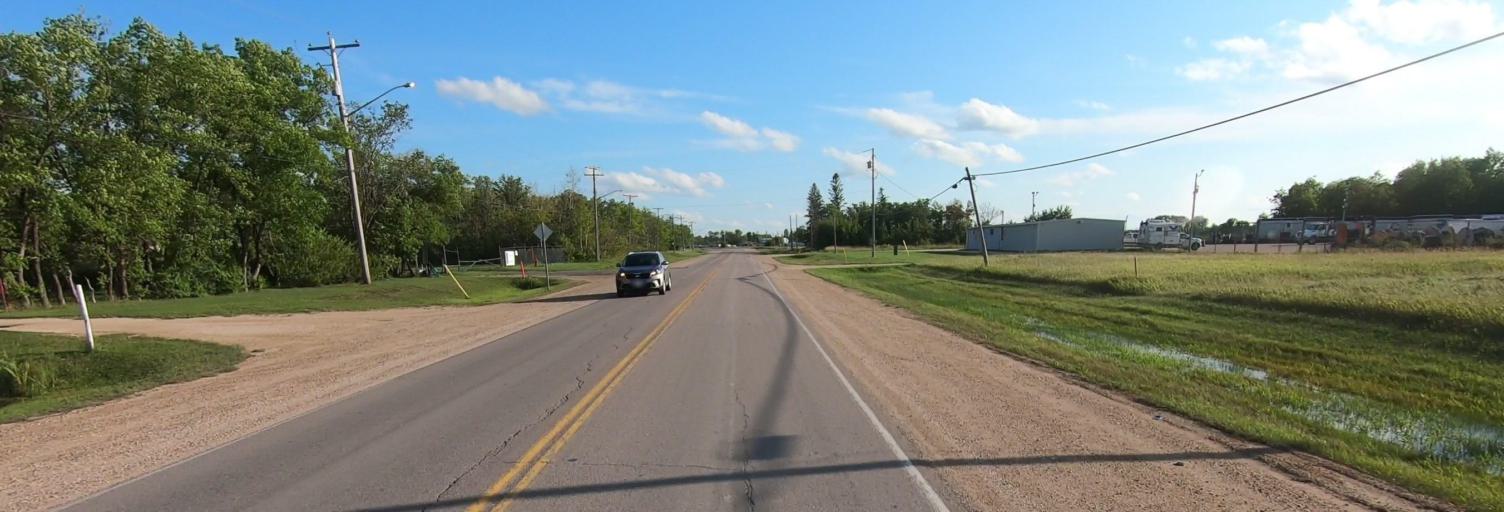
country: CA
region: Manitoba
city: Selkirk
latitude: 50.1612
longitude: -96.8677
